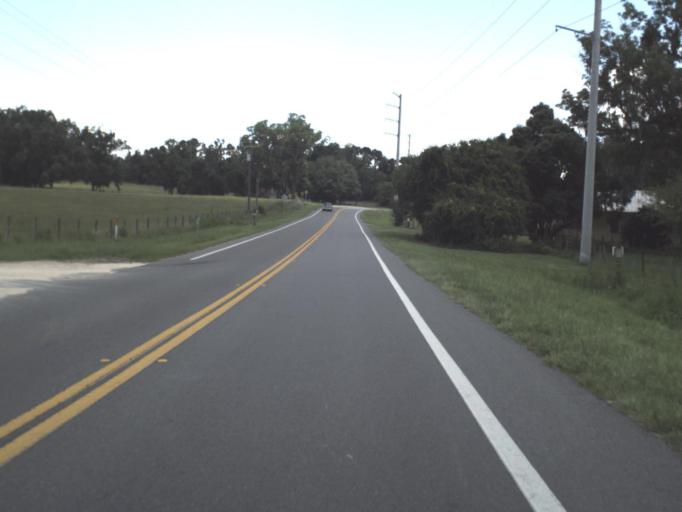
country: US
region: Florida
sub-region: Alachua County
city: Hawthorne
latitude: 29.6767
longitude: -82.0340
